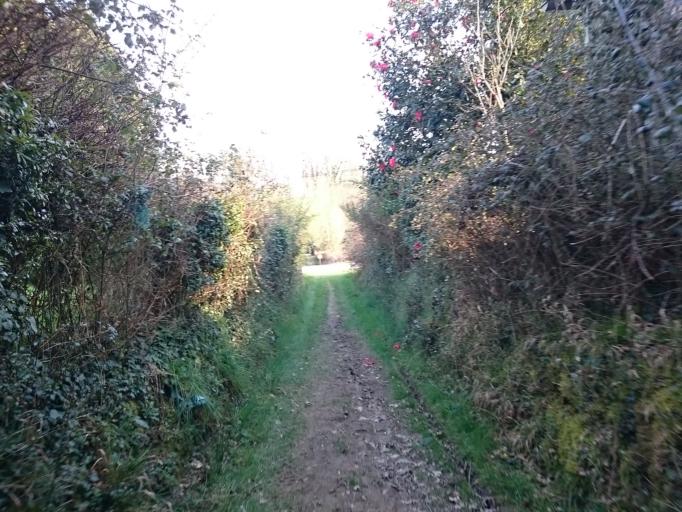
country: FR
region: Brittany
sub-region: Departement d'Ille-et-Vilaine
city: Chanteloup
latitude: 47.9356
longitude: -1.6092
